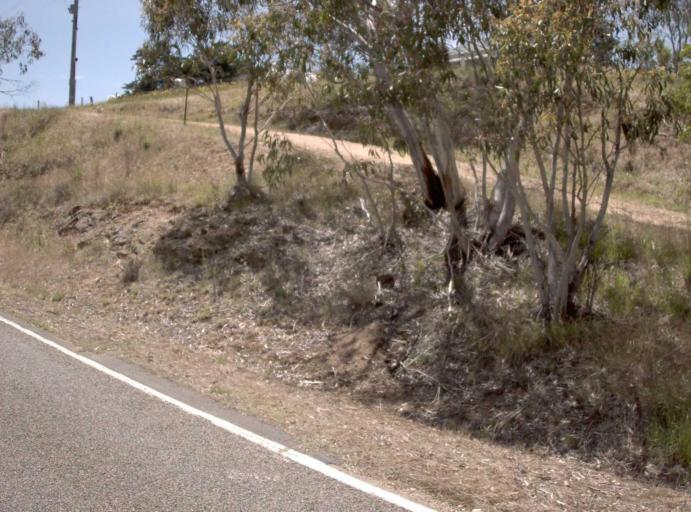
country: AU
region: Victoria
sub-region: Alpine
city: Mount Beauty
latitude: -37.1080
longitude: 147.5797
